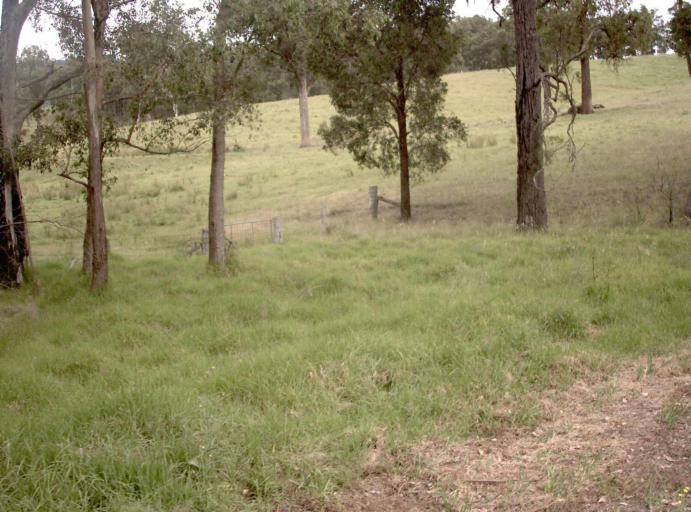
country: AU
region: Victoria
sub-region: East Gippsland
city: Bairnsdale
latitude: -37.7216
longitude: 147.5912
